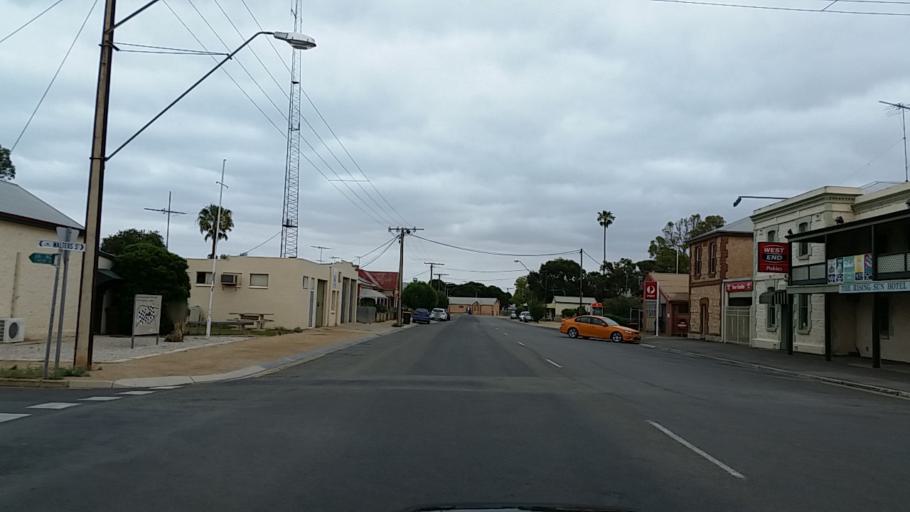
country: AU
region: South Australia
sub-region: Wakefield
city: Balaklava
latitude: -34.1850
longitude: 138.1486
